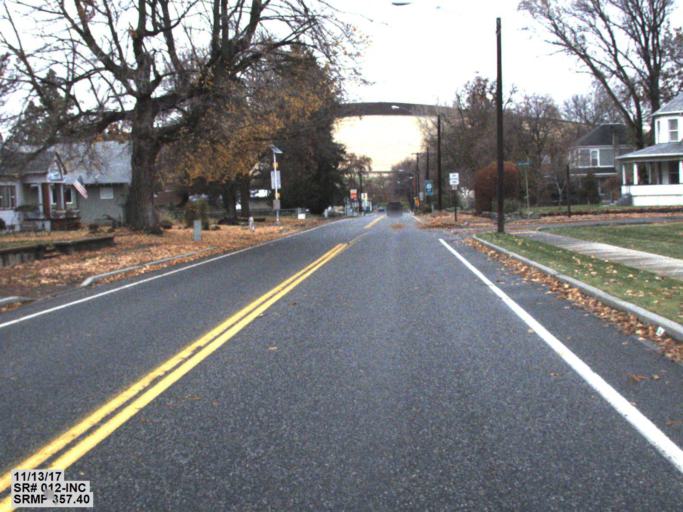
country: US
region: Washington
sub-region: Walla Walla County
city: Waitsburg
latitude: 46.2675
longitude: -118.1532
